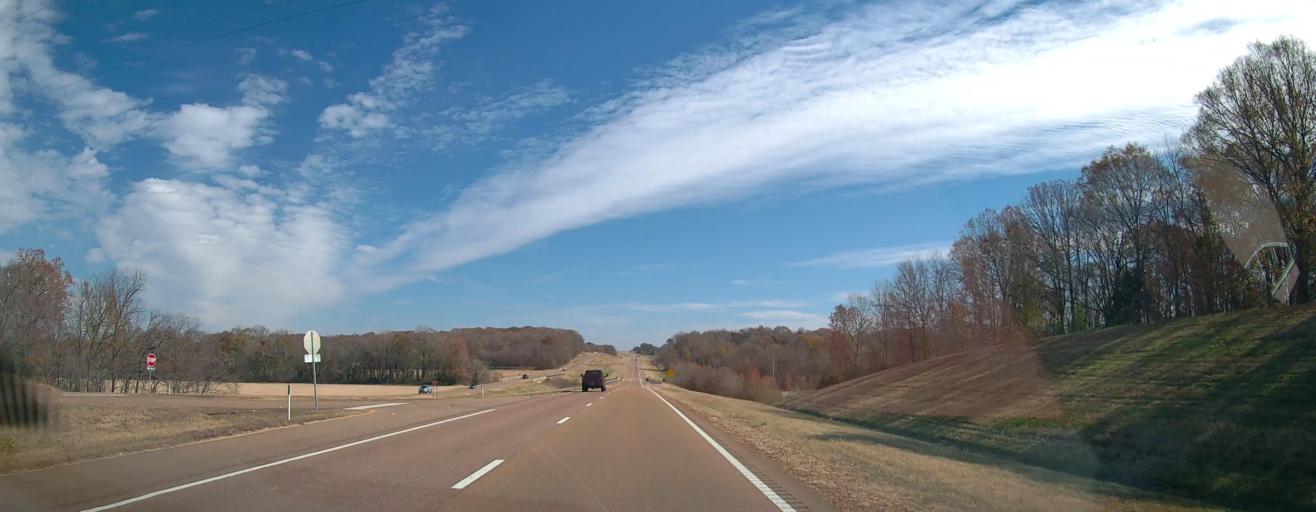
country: US
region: Mississippi
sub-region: Marshall County
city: Holly Springs
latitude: 34.9460
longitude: -89.3474
